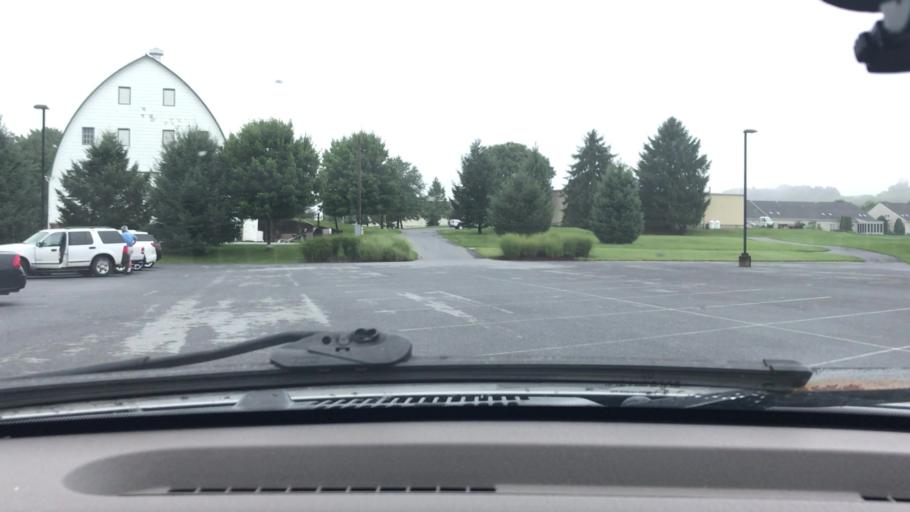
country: US
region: Pennsylvania
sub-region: Dauphin County
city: Palmdale
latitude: 40.2984
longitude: -76.6316
